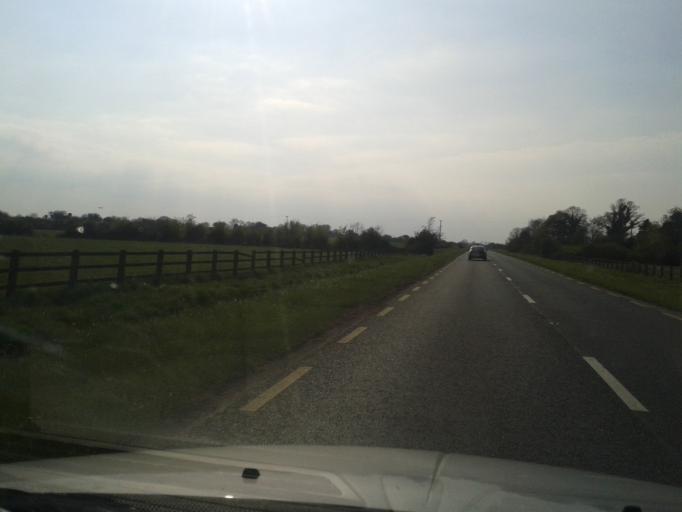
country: IE
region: Leinster
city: Ballymun
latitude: 53.4385
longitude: -6.2695
